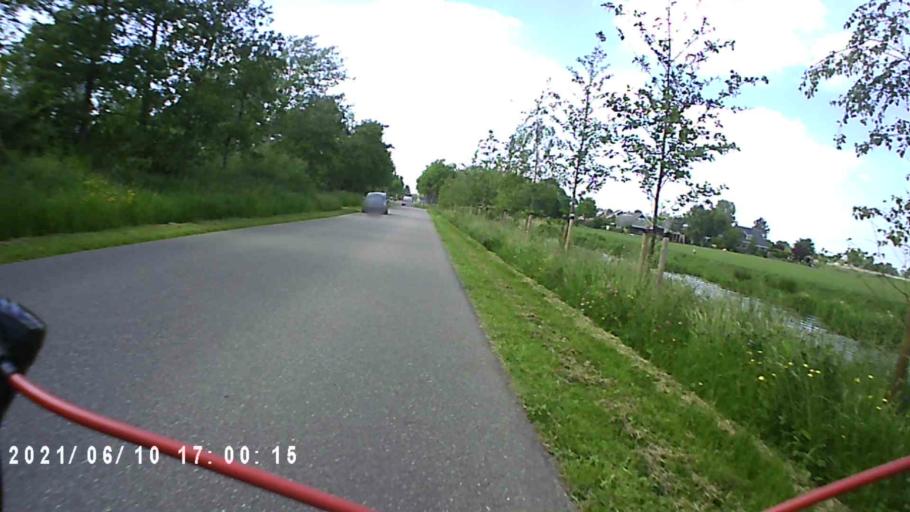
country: NL
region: Friesland
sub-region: Gemeente Kollumerland en Nieuwkruisland
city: Kollum
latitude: 53.2712
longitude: 6.1573
